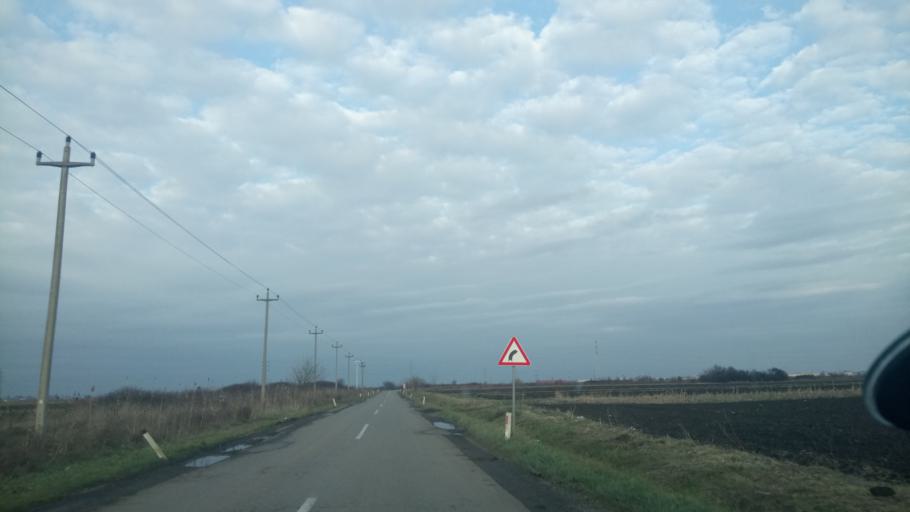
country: RS
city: Vojka
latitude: 44.9435
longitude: 20.1726
